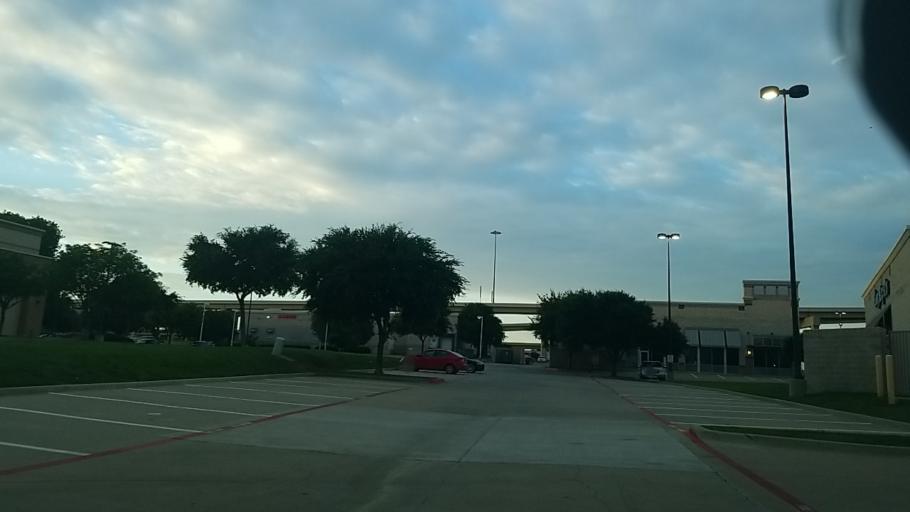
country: US
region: Texas
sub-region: Denton County
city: Lewisville
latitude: 32.9999
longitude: -96.9644
